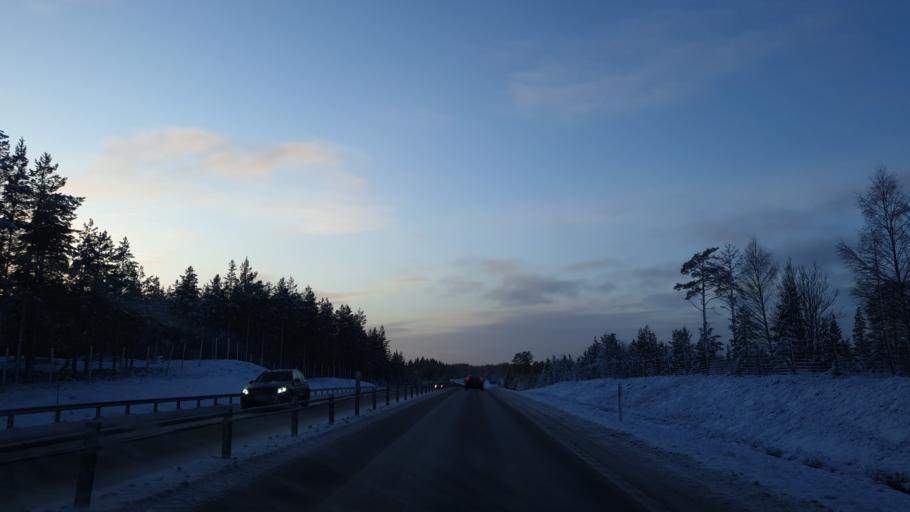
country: SE
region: Vaesterbotten
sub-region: Umea Kommun
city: Hoernefors
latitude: 63.6463
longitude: 19.9374
